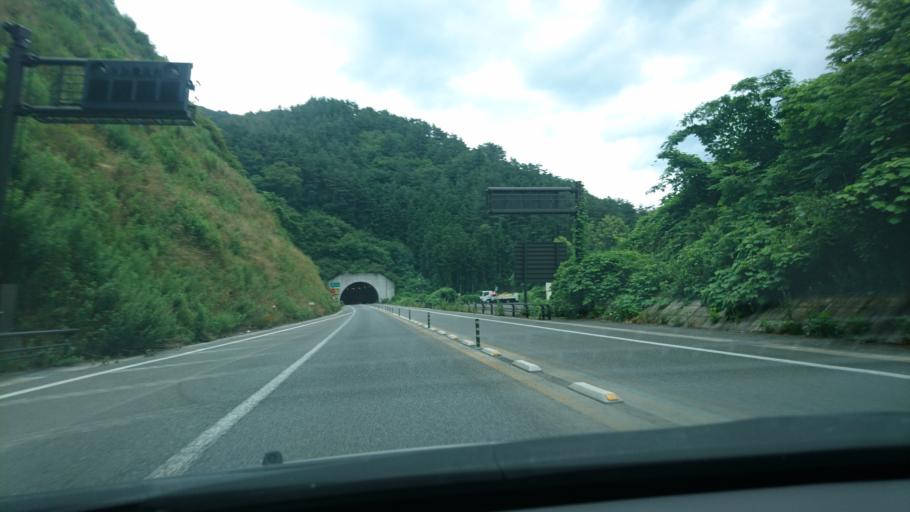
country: JP
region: Iwate
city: Kamaishi
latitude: 39.3020
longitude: 141.8750
